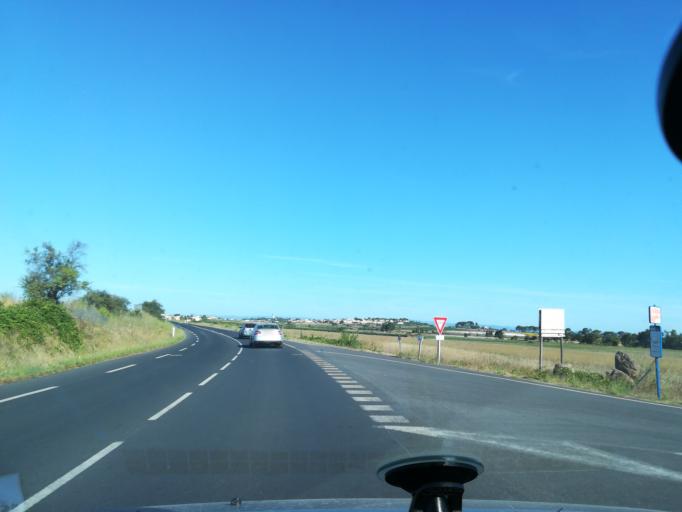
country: FR
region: Languedoc-Roussillon
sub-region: Departement de l'Herault
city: Portiragnes
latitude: 43.2933
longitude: 3.3603
